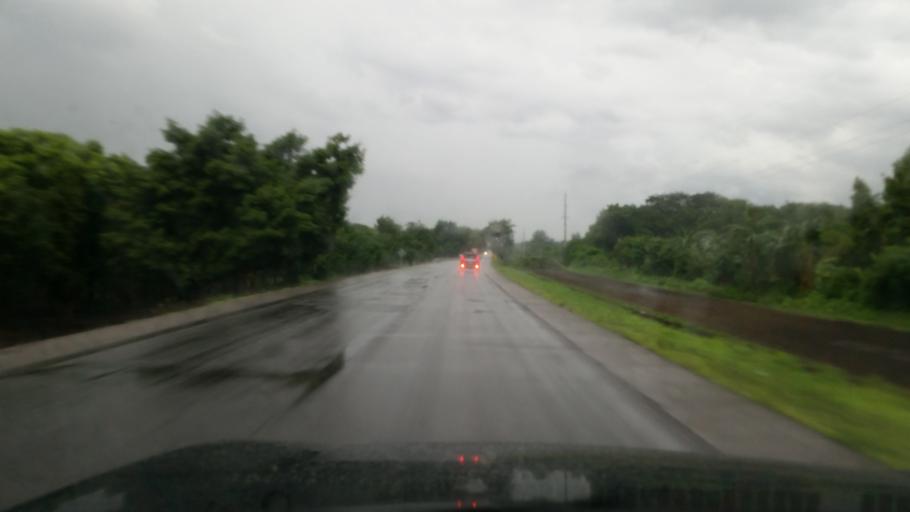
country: NI
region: Chinandega
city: Puerto Morazan
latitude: 12.7956
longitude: -86.9798
